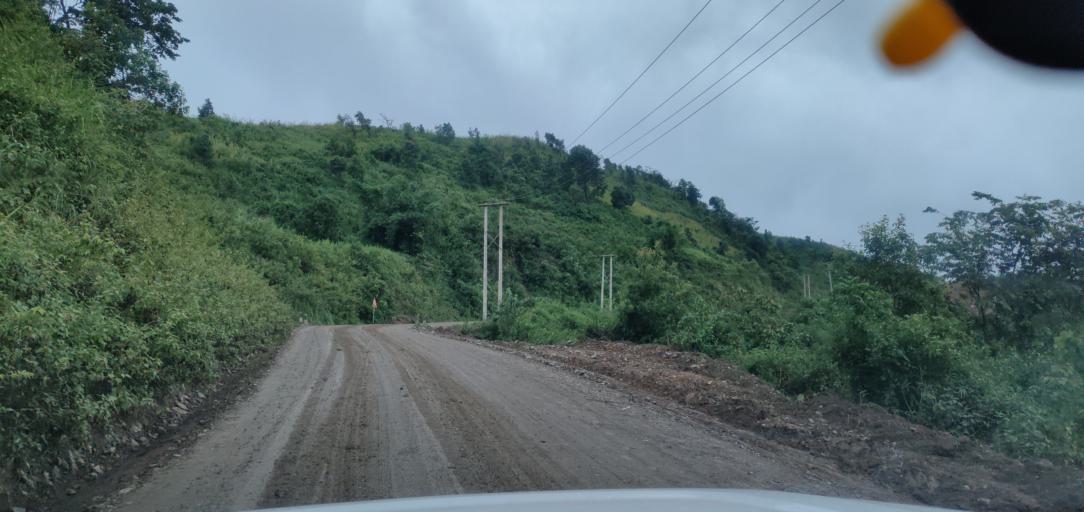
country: LA
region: Phongsali
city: Phongsali
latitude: 21.4273
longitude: 102.1689
